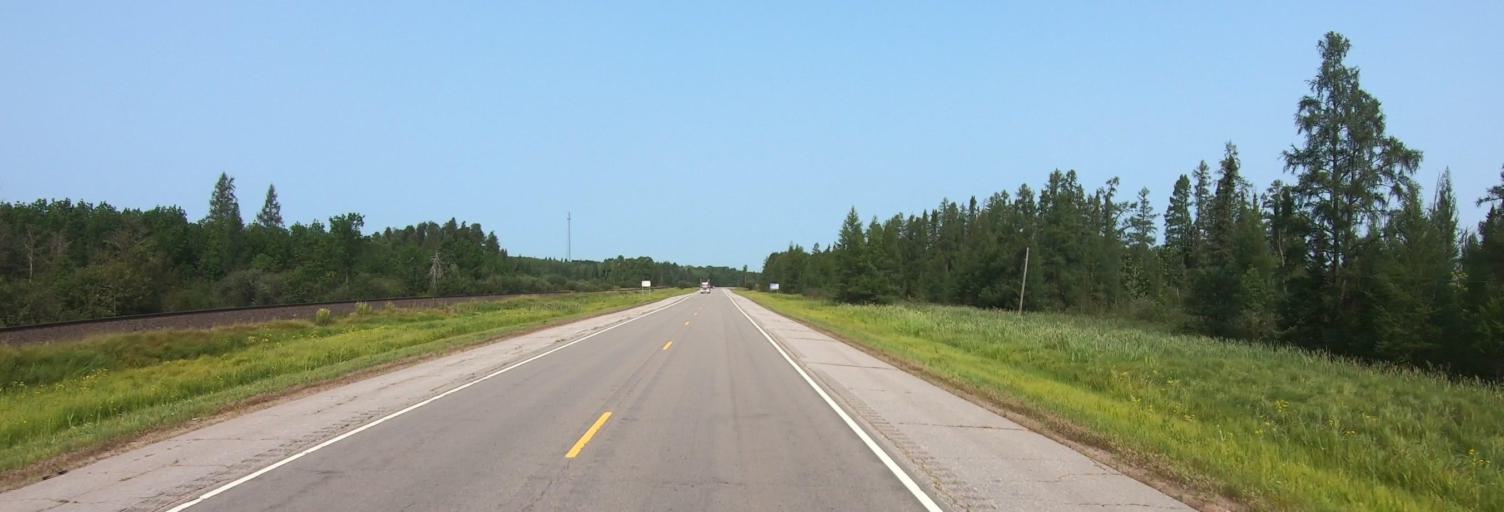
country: US
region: Minnesota
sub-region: Saint Louis County
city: Chisholm
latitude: 48.1440
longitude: -92.8608
